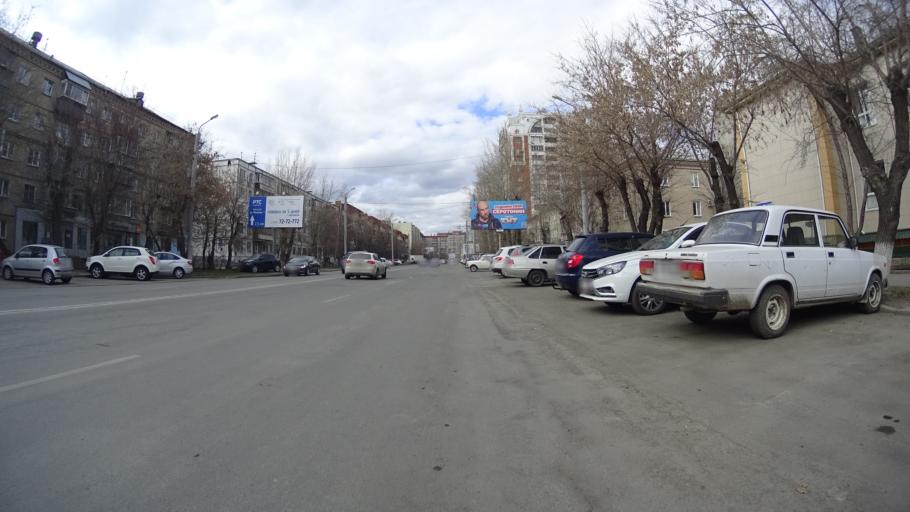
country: RU
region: Chelyabinsk
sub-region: Gorod Chelyabinsk
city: Chelyabinsk
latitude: 55.1496
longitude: 61.3806
